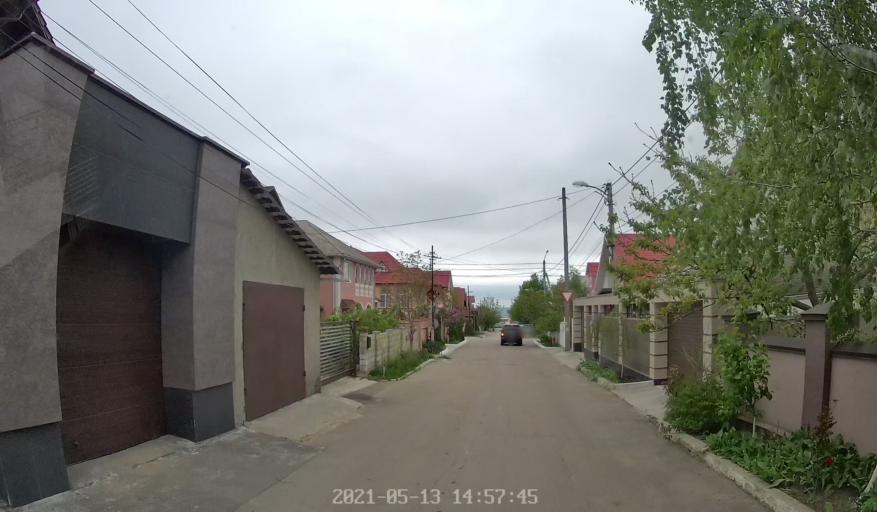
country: MD
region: Chisinau
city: Stauceni
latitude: 47.1014
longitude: 28.8712
